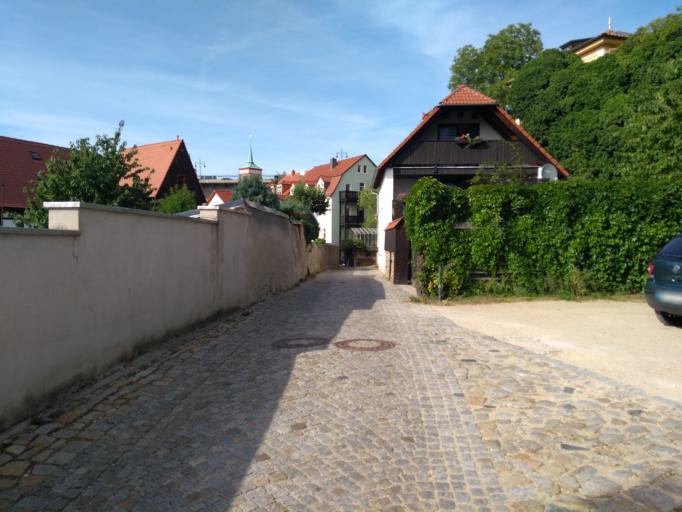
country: DE
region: Saxony
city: Bautzen
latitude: 51.1784
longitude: 14.4218
